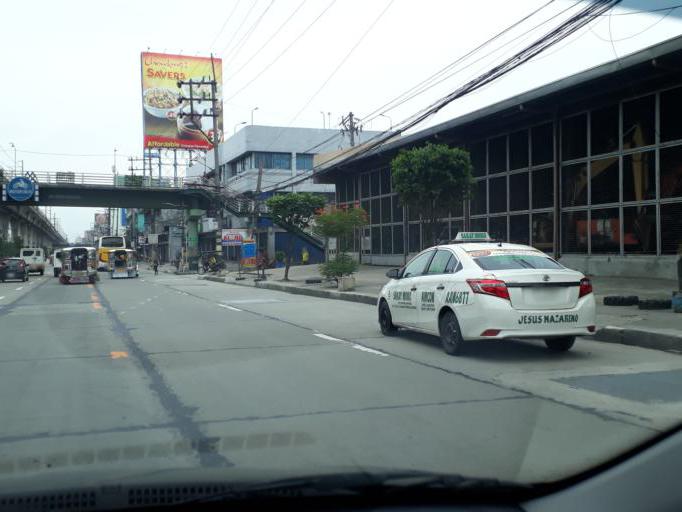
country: PH
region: Calabarzon
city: Del Monte
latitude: 14.6575
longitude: 120.9938
